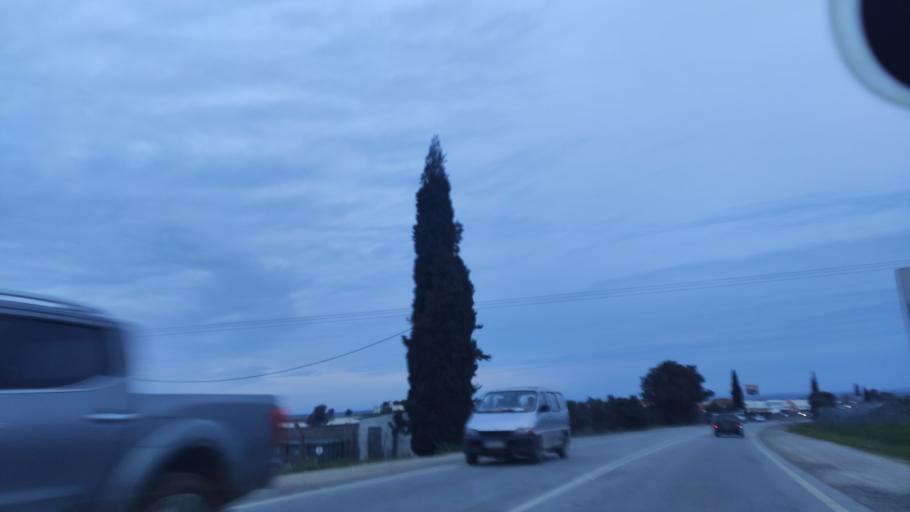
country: PT
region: Beja
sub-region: Beja
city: Beja
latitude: 38.0263
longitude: -7.8649
